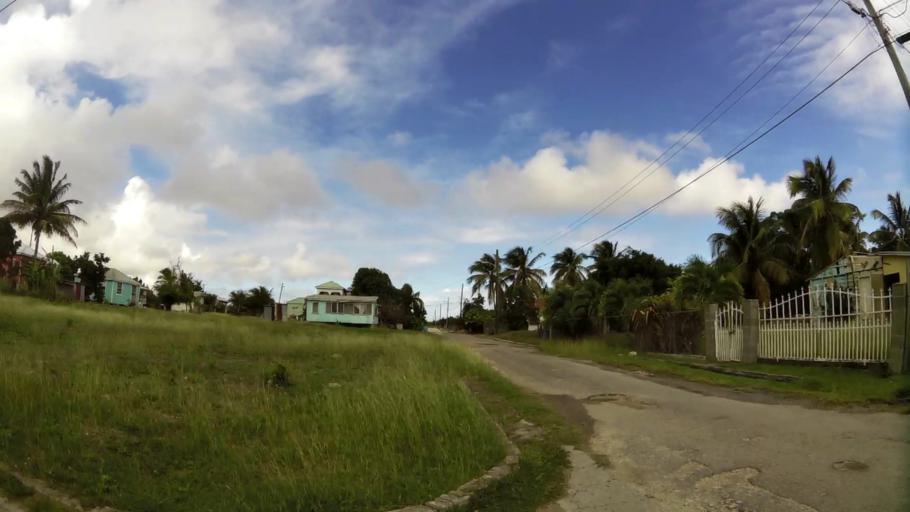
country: AG
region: Saint Paul
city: Liberta
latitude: 17.0464
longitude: -61.7504
